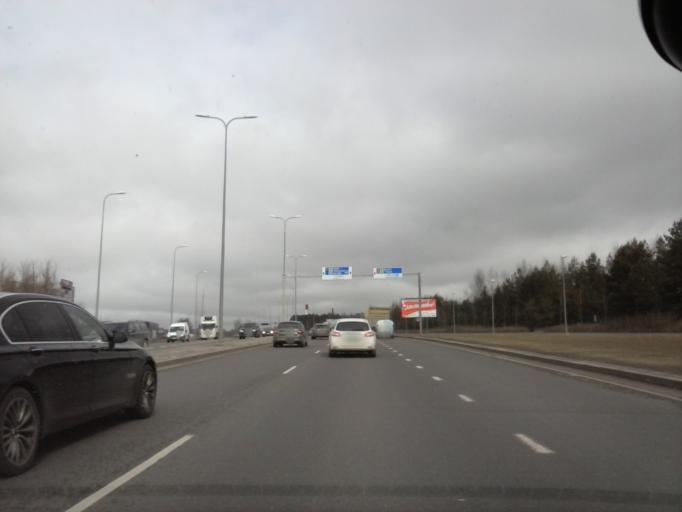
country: EE
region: Harju
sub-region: Tallinna linn
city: Tallinn
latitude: 59.4108
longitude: 24.7556
